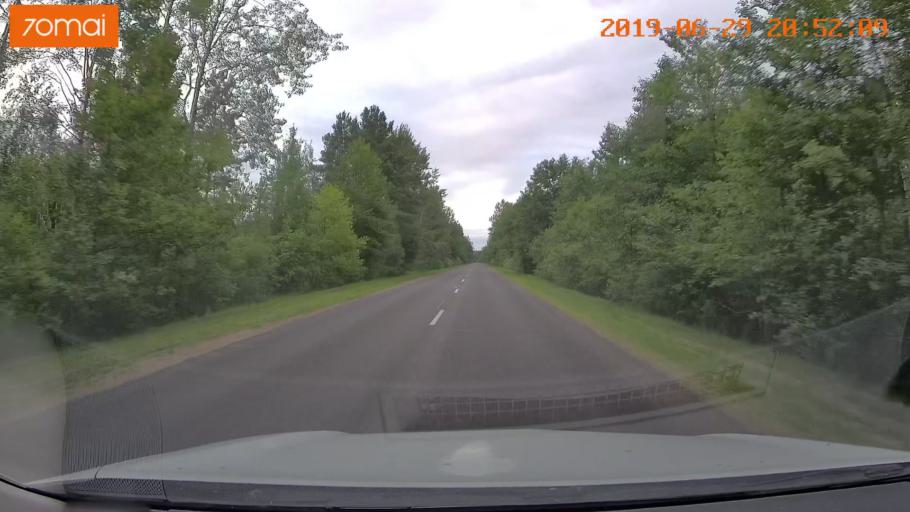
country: BY
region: Brest
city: Hantsavichy
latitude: 52.6962
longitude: 26.3590
